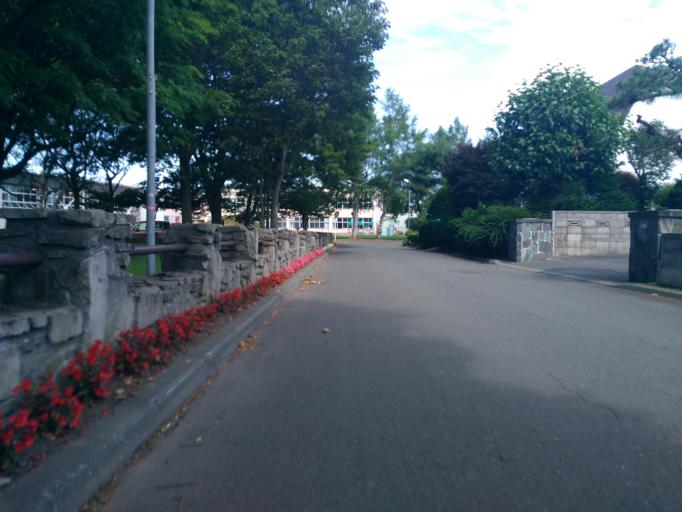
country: JP
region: Hokkaido
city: Ebetsu
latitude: 43.0798
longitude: 141.5026
